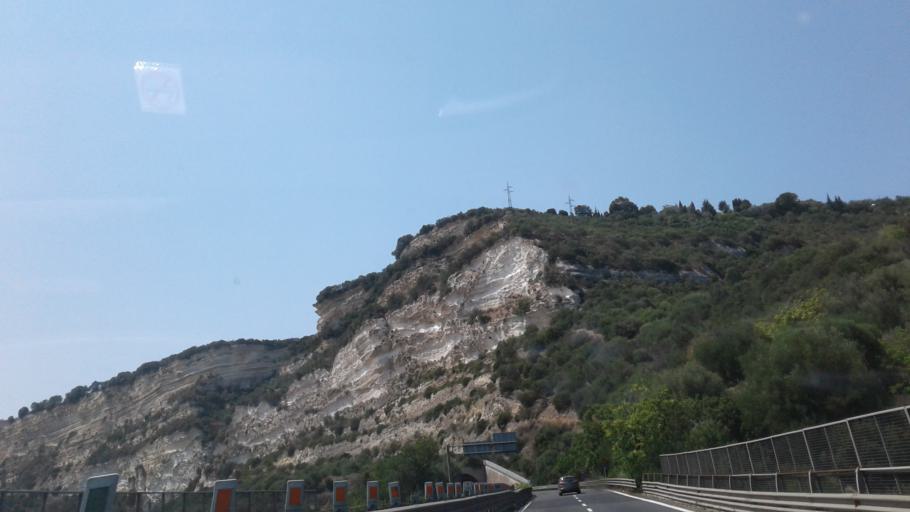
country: IT
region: Sardinia
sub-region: Provincia di Sassari
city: Ossi
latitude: 40.7003
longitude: 8.5911
